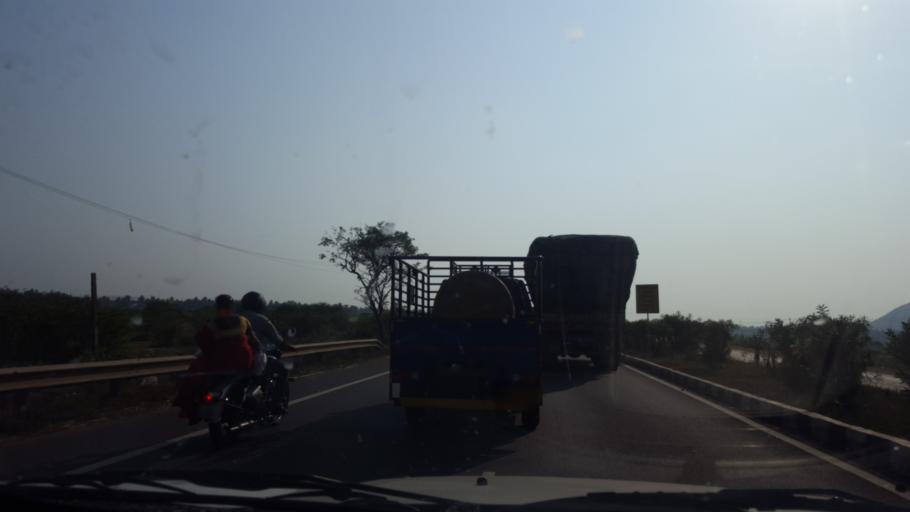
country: IN
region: Andhra Pradesh
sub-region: Vishakhapatnam
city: Etikoppaka
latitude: 17.4415
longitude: 82.7529
